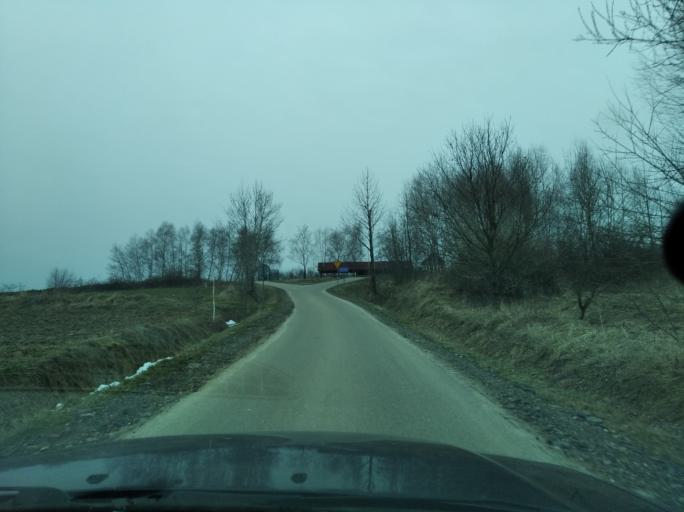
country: PL
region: Subcarpathian Voivodeship
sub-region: Powiat rzeszowski
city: Siedliska
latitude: 49.9338
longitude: 21.9615
